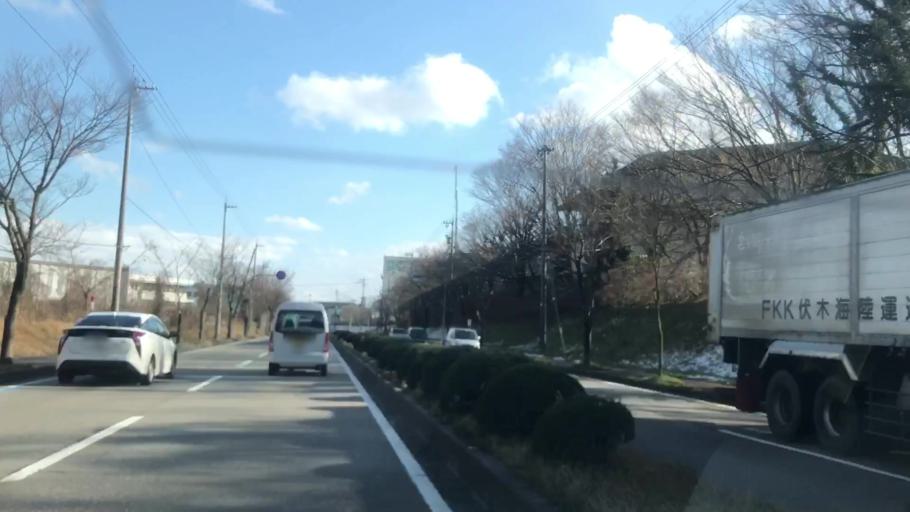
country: JP
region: Toyama
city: Takaoka
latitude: 36.6993
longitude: 137.0651
